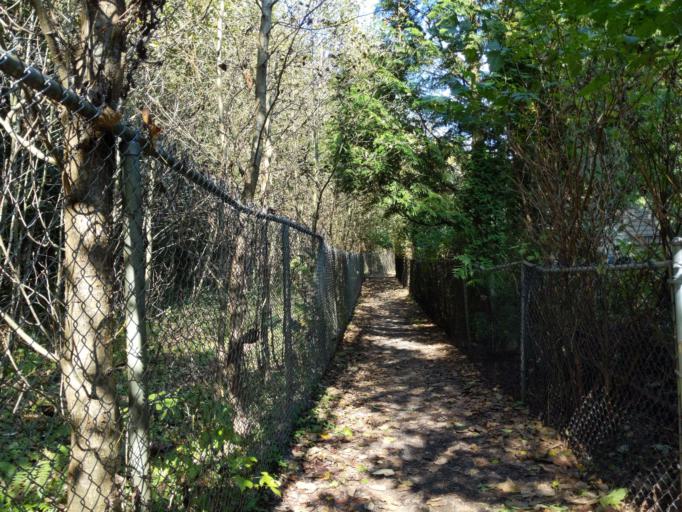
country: CA
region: British Columbia
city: Langley
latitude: 49.0873
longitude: -122.6797
